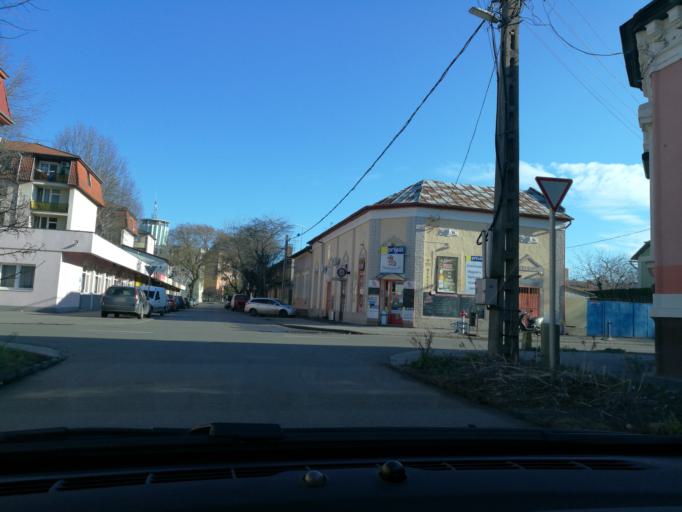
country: HU
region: Szabolcs-Szatmar-Bereg
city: Nyiregyhaza
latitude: 47.9466
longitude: 21.7119
